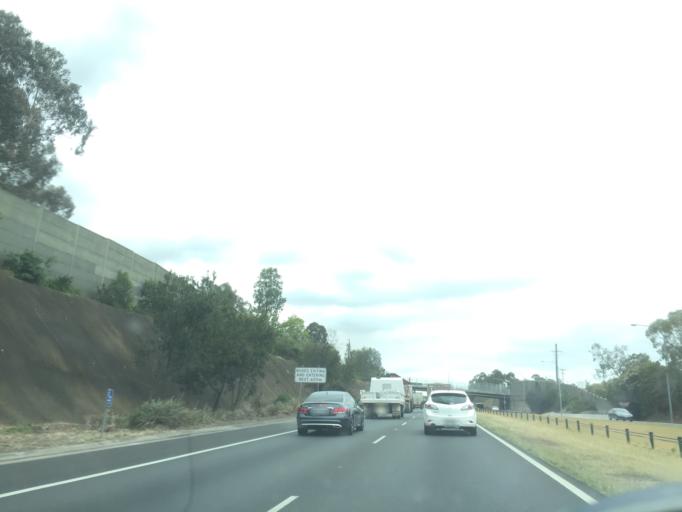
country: AU
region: New South Wales
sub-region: Parramatta
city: Northmead
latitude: -33.7716
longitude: 150.9830
